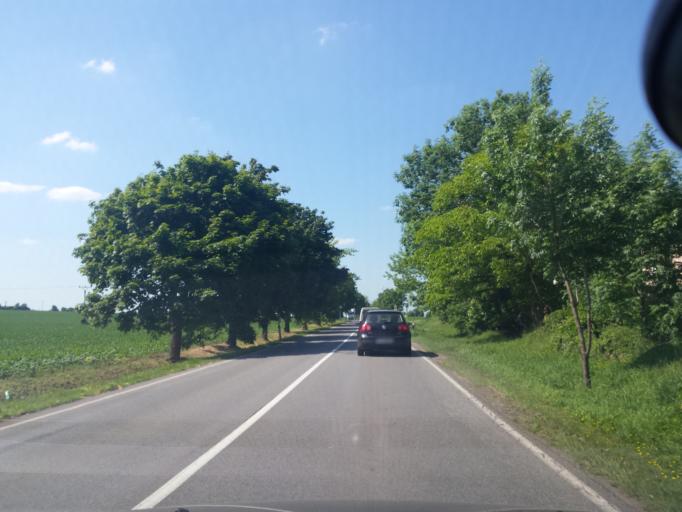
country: CZ
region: Central Bohemia
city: Velke Prilepy
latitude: 50.1933
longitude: 14.3204
